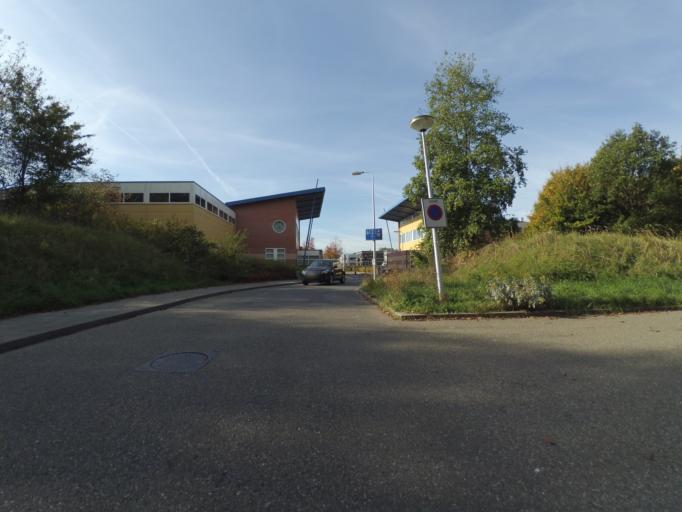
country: NL
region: Gelderland
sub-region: Gemeente Lochem
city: Epse
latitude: 52.2416
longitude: 6.2235
